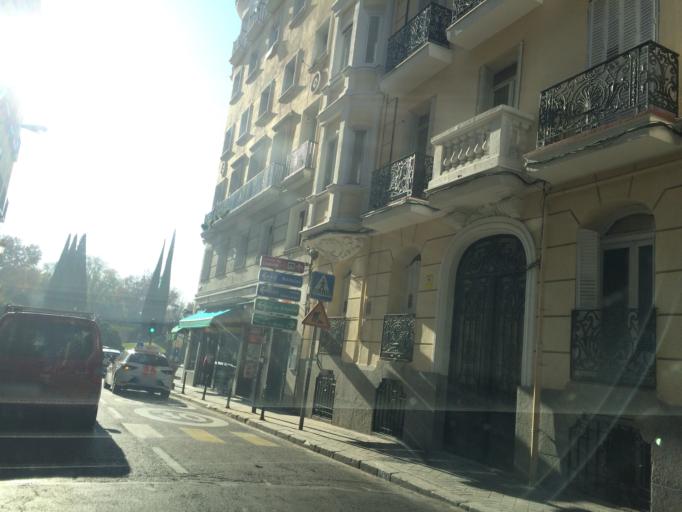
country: ES
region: Madrid
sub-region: Provincia de Madrid
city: City Center
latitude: 40.4252
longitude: -3.7156
